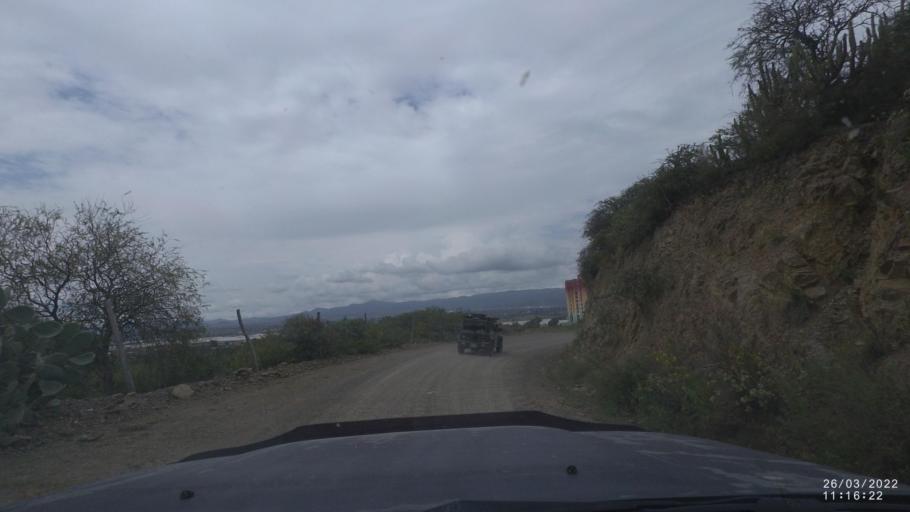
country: BO
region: Cochabamba
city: Tarata
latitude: -17.5342
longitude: -66.0224
